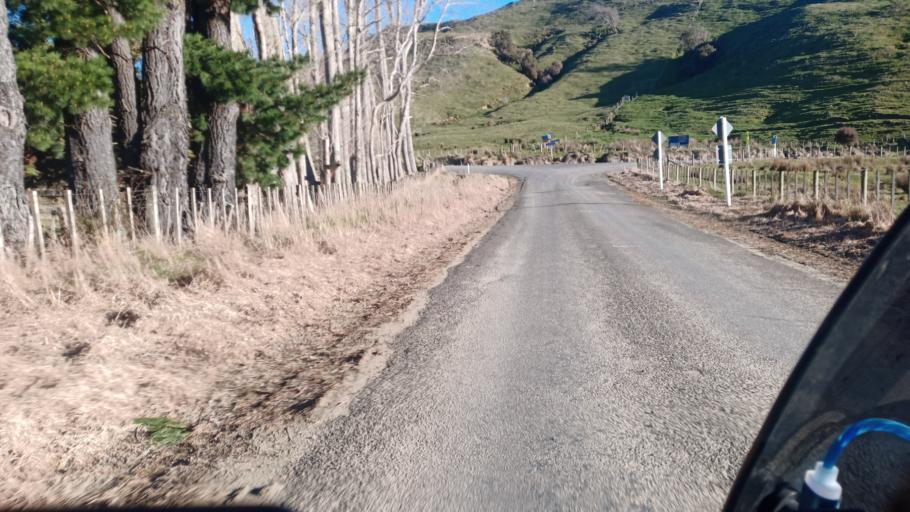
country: NZ
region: Bay of Plenty
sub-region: Opotiki District
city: Opotiki
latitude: -38.4615
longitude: 177.4234
